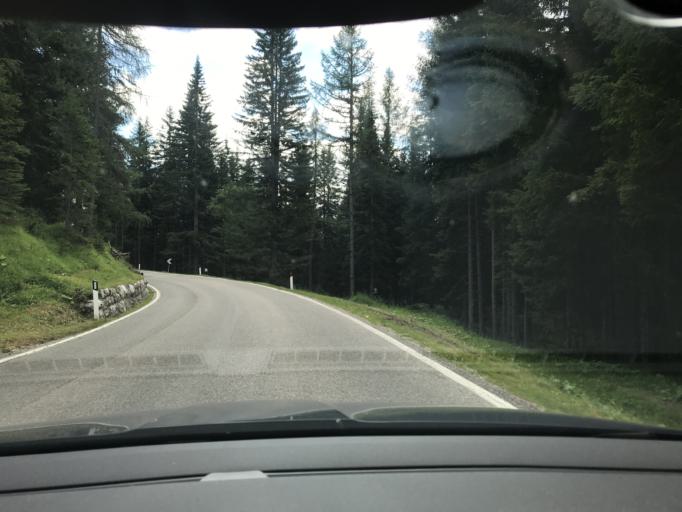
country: IT
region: Veneto
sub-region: Provincia di Belluno
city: Cortina d'Ampezzo
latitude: 46.5578
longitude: 12.2193
